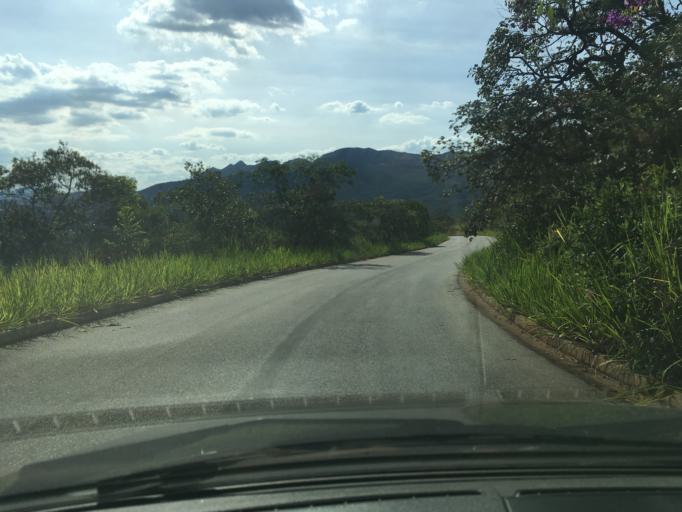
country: BR
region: Minas Gerais
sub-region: Ibirite
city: Ibirite
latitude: -20.1260
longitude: -44.0664
